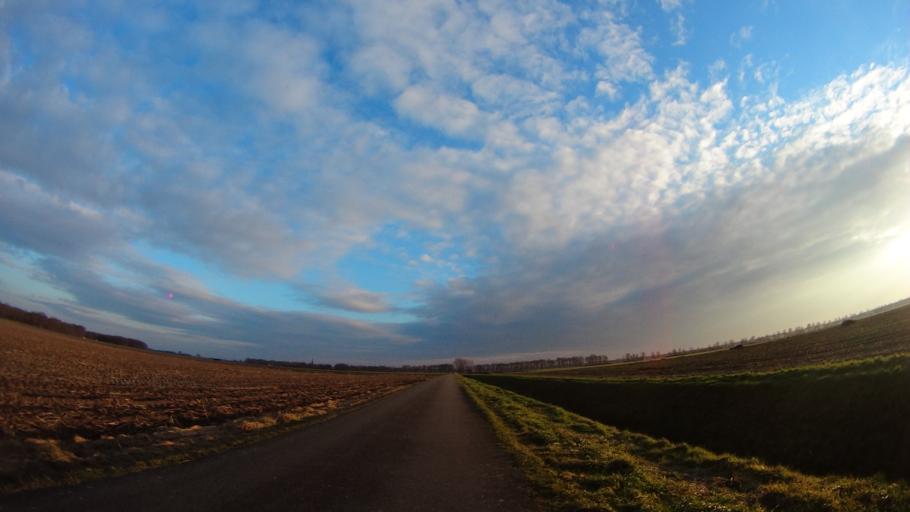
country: NL
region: Drenthe
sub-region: Gemeente Coevorden
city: Sleen
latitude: 52.7866
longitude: 6.7836
